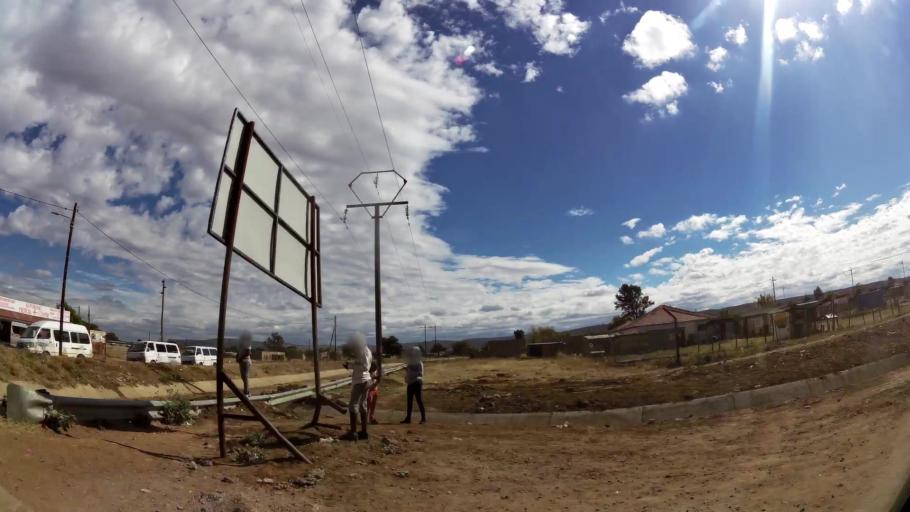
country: ZA
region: Limpopo
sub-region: Waterberg District Municipality
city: Bela-Bela
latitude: -24.8791
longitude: 28.3218
